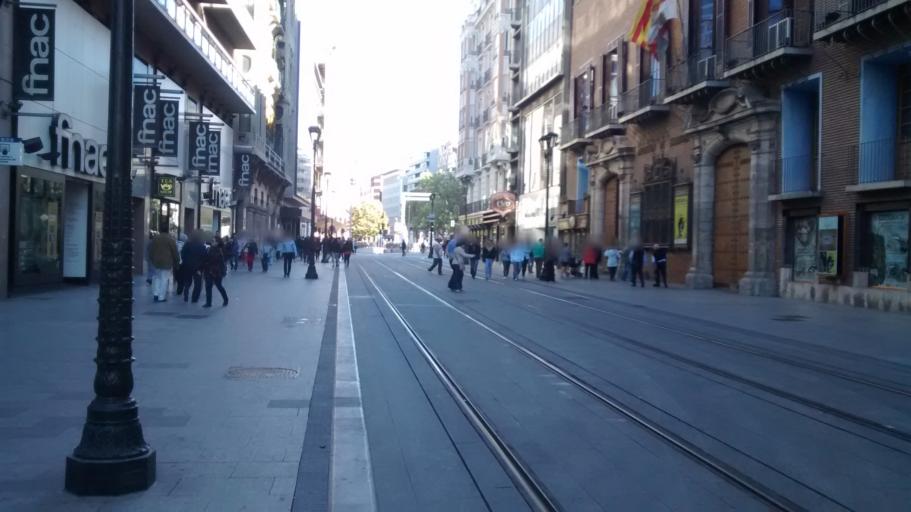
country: ES
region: Aragon
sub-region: Provincia de Zaragoza
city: Zaragoza
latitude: 41.6531
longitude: -0.8821
